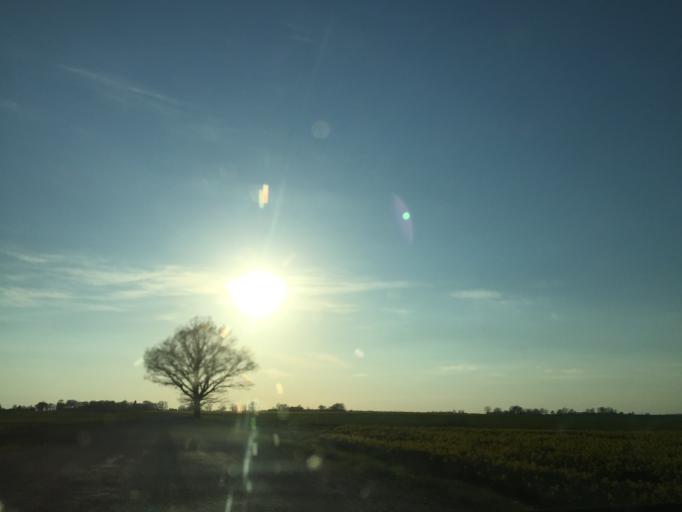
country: LV
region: Bauskas Rajons
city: Bauska
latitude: 56.2849
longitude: 24.2427
